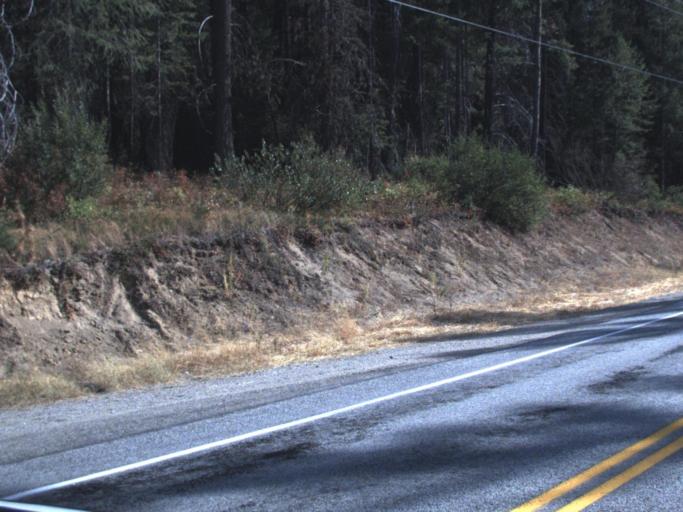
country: US
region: Washington
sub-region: Pend Oreille County
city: Newport
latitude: 48.1536
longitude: -117.3037
